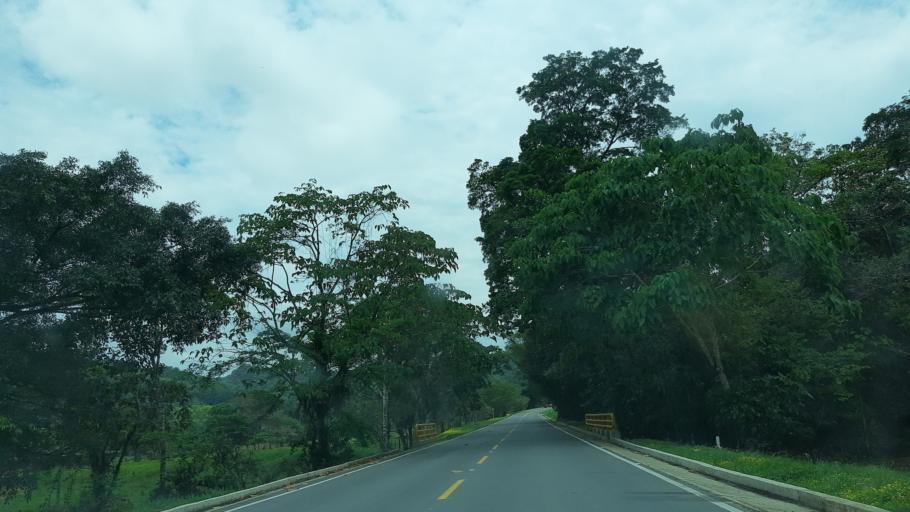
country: CO
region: Boyaca
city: San Luis de Gaceno
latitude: 4.8299
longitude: -73.1446
